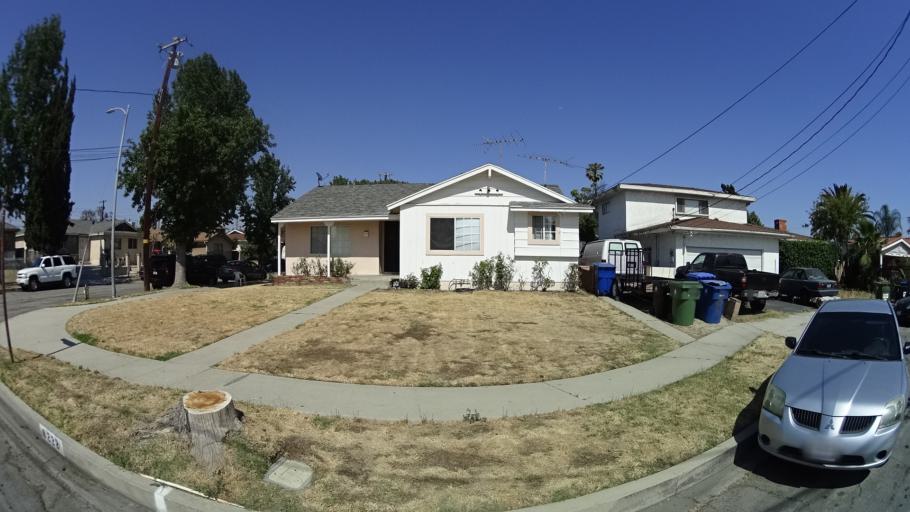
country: US
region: California
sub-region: Los Angeles County
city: Van Nuys
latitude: 34.2206
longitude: -118.4184
